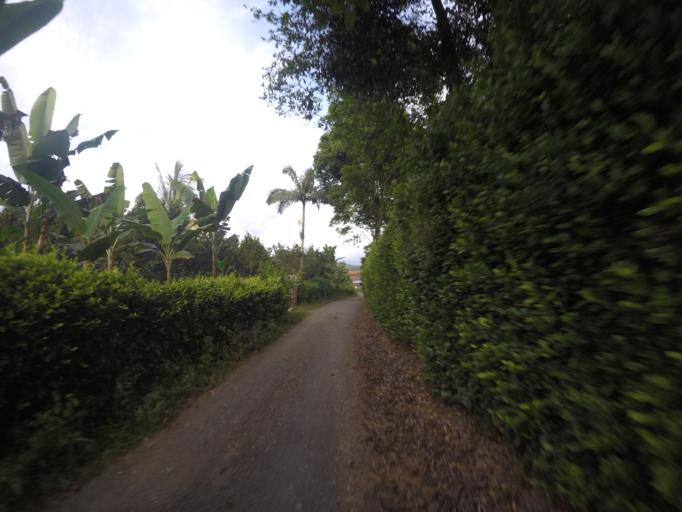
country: CO
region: Valle del Cauca
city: Ulloa
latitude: 4.7127
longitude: -75.7288
